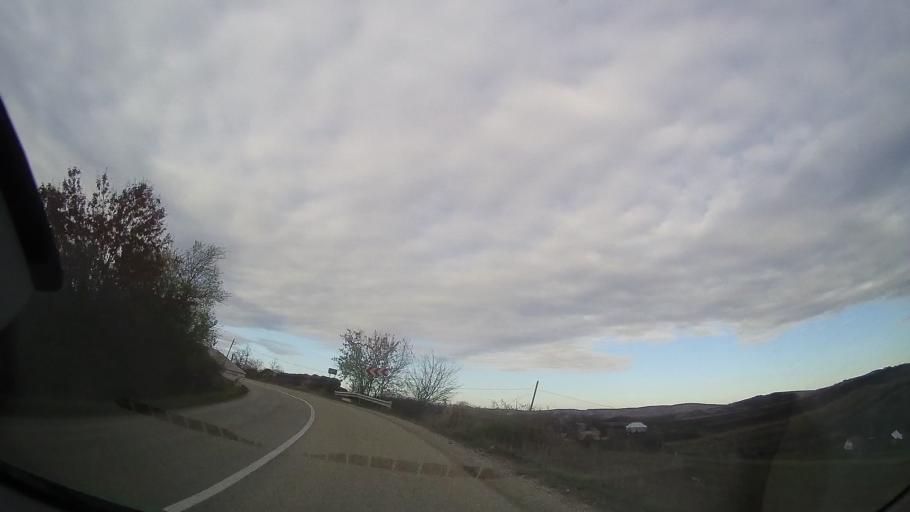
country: RO
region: Bistrita-Nasaud
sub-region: Comuna Budesti
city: Budesti
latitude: 46.8922
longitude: 24.2498
